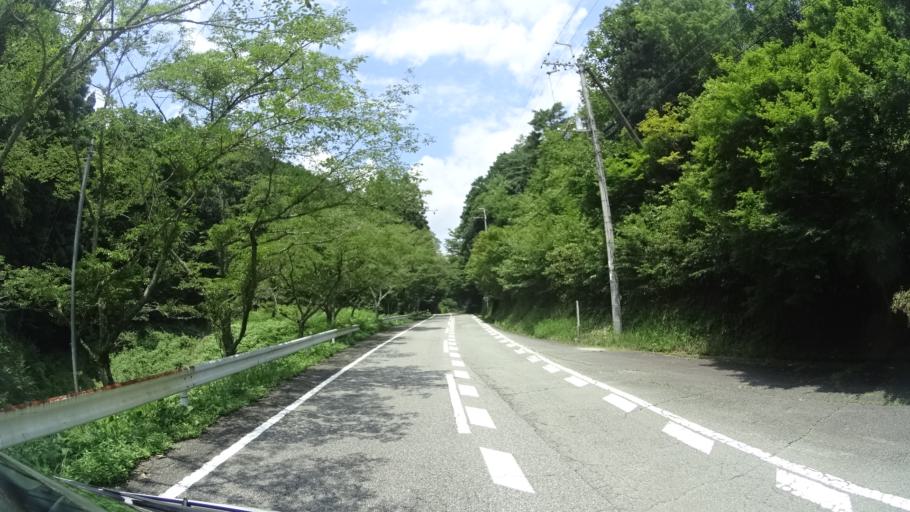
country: JP
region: Hyogo
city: Sasayama
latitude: 35.1733
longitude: 135.2479
